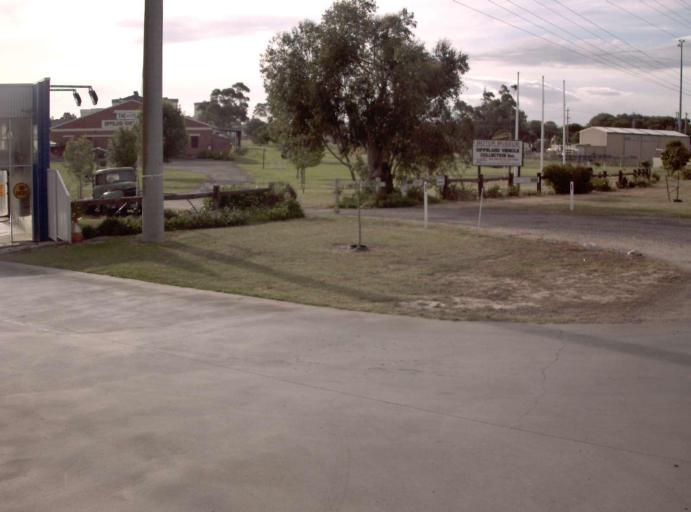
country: AU
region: Victoria
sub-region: Wellington
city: Sale
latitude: -37.9730
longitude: 146.9848
